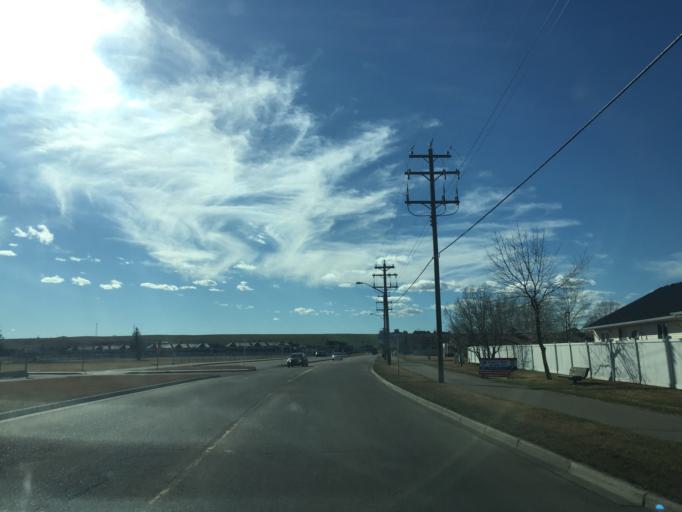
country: CA
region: Alberta
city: Airdrie
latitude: 51.2928
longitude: -114.0341
